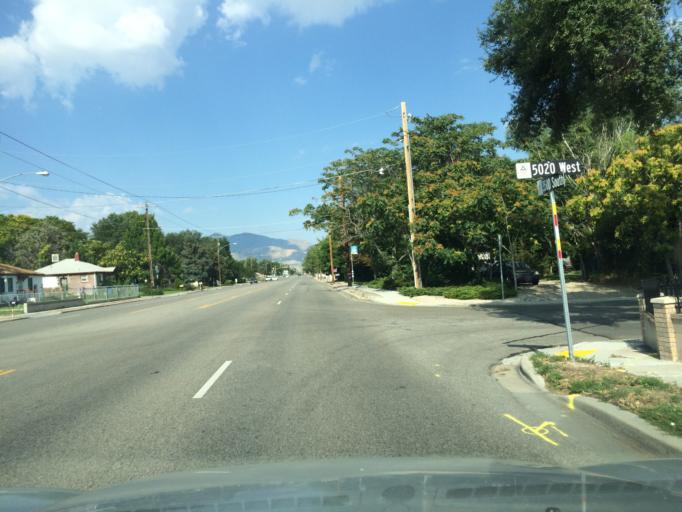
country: US
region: Utah
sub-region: Salt Lake County
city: West Valley City
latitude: 40.6966
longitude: -112.0105
